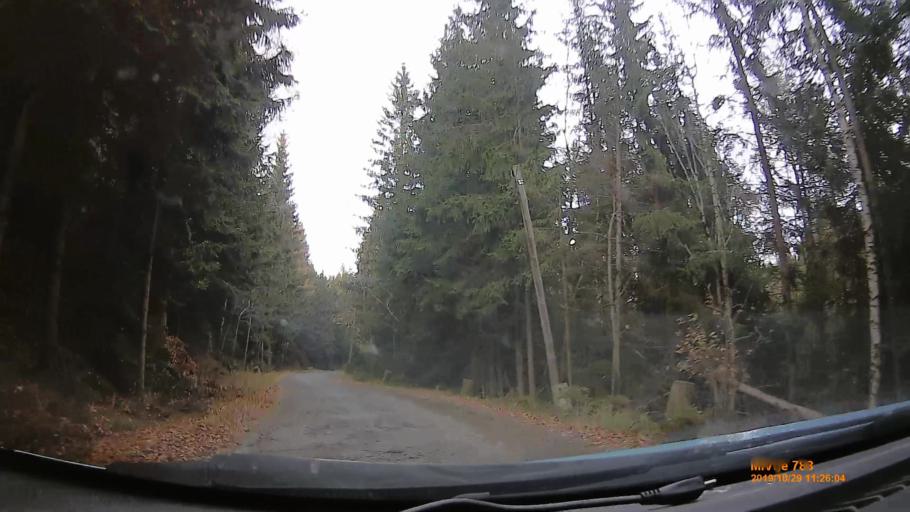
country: PL
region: Lower Silesian Voivodeship
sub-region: Powiat klodzki
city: Szczytna
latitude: 50.4447
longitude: 16.4207
